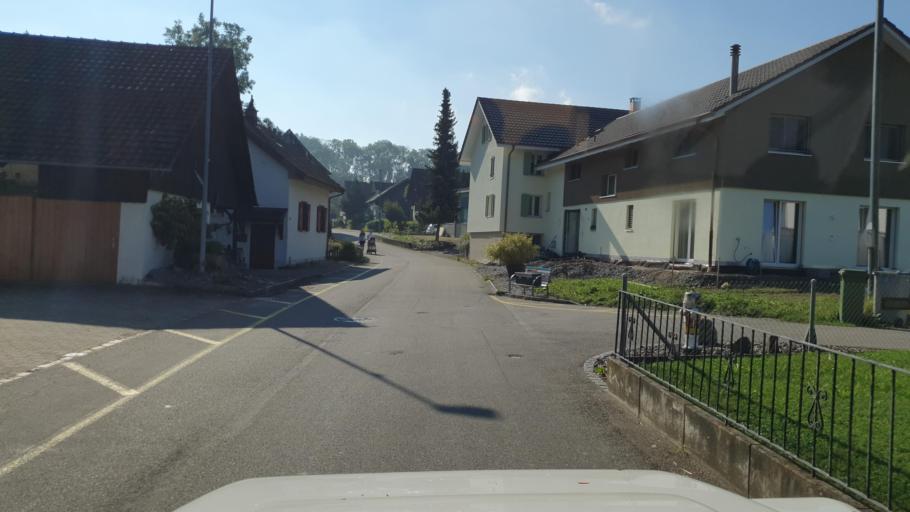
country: CH
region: Aargau
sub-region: Bezirk Bremgarten
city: Sarmenstorf
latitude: 47.3273
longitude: 8.2676
